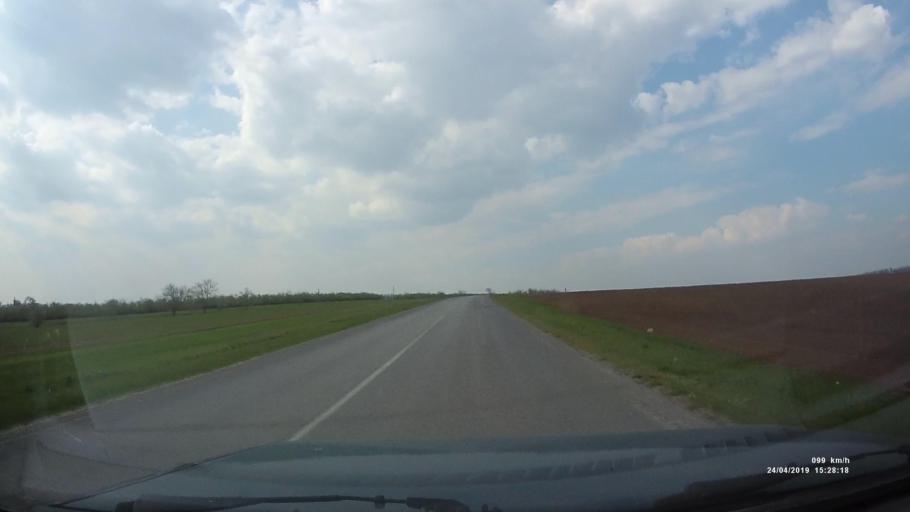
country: RU
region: Rostov
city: Remontnoye
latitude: 46.5770
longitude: 43.0193
